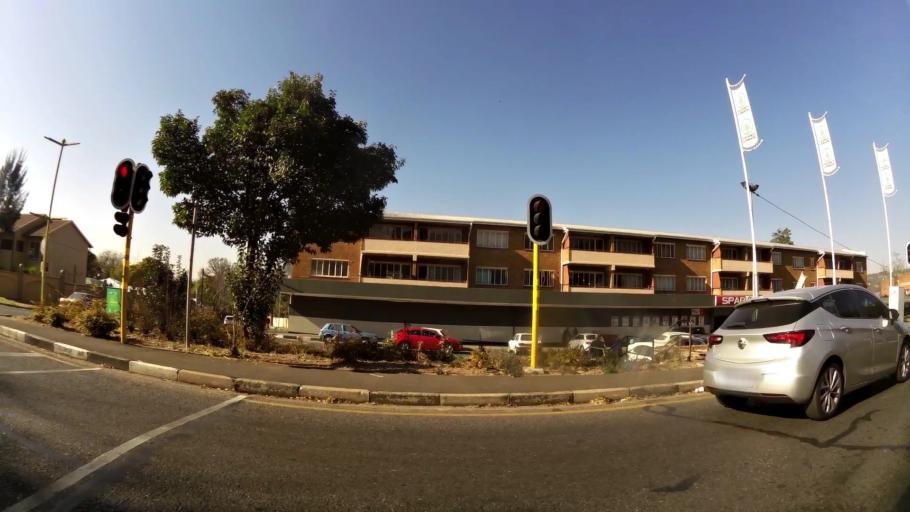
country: ZA
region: Gauteng
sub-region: City of Johannesburg Metropolitan Municipality
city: Modderfontein
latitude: -26.1441
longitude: 28.1097
